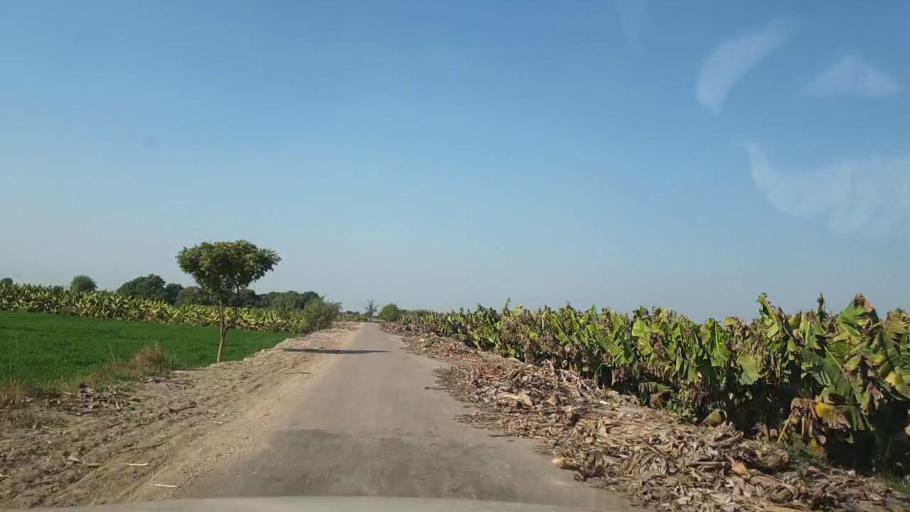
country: PK
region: Sindh
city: Tando Allahyar
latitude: 25.4793
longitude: 68.6601
